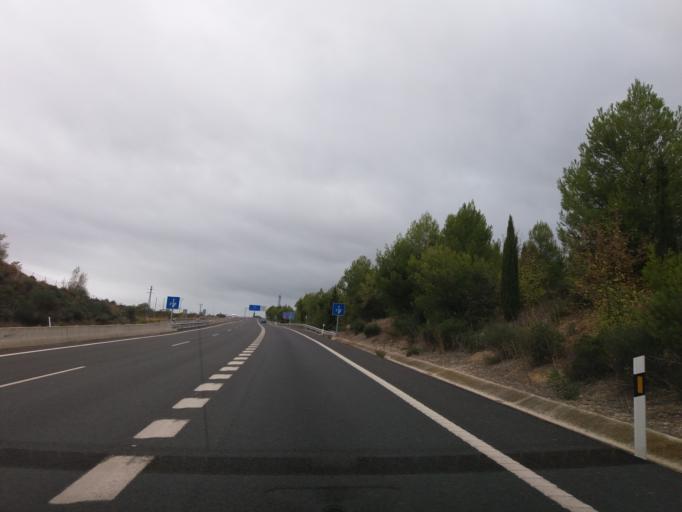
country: ES
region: Navarre
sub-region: Provincia de Navarra
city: Ayegui
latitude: 42.6494
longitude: -2.0162
